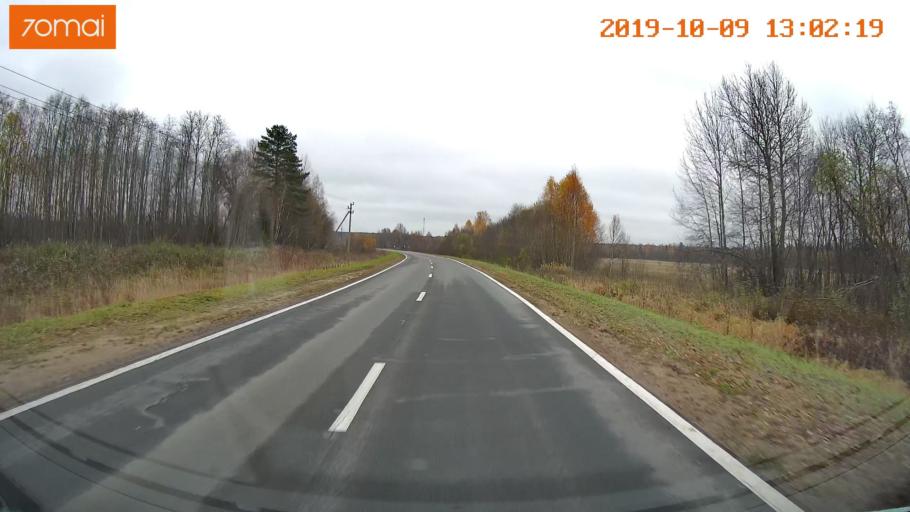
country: RU
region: Jaroslavl
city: Prechistoye
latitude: 58.3623
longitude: 40.4986
